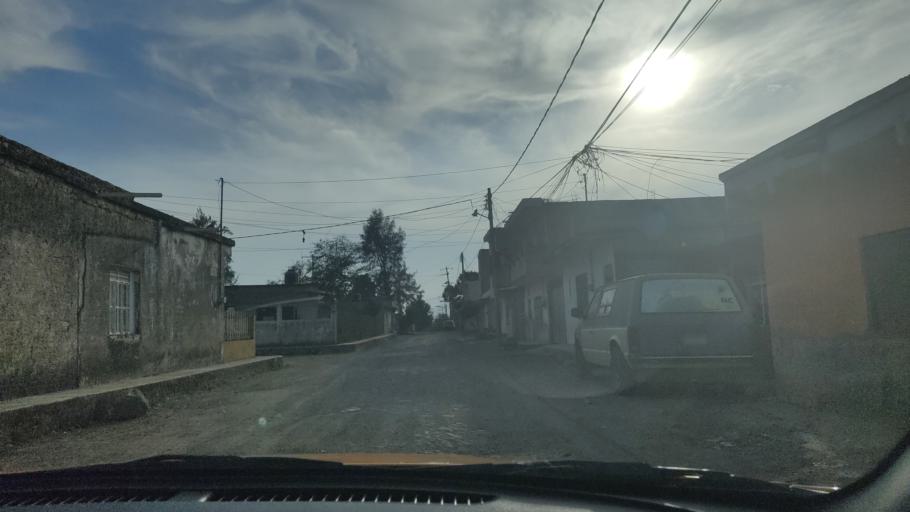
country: MX
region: Nayarit
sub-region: Tepic
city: La Corregidora
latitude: 21.4507
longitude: -104.8214
